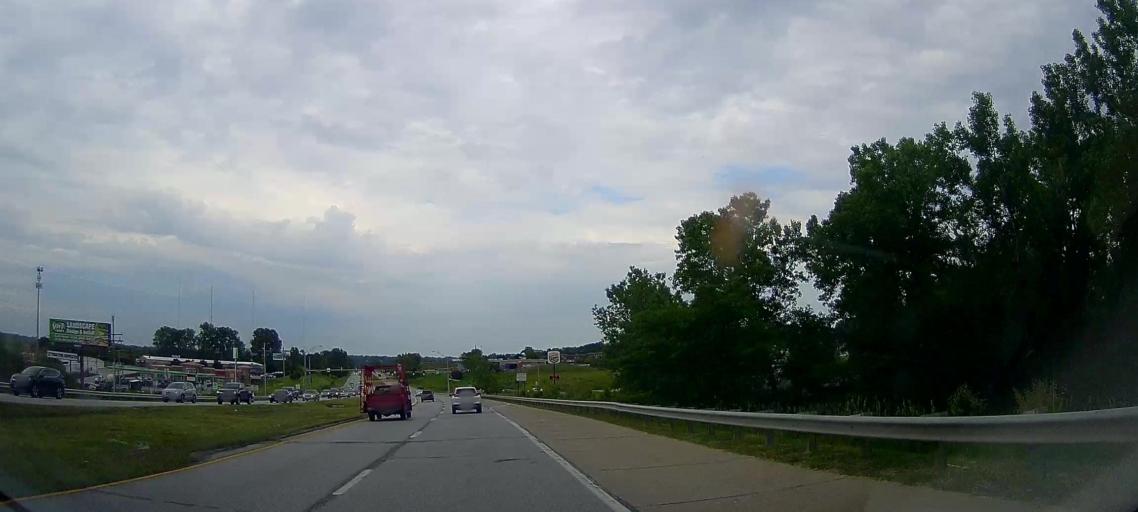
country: US
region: Nebraska
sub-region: Douglas County
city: Bennington
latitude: 41.3199
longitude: -96.0666
